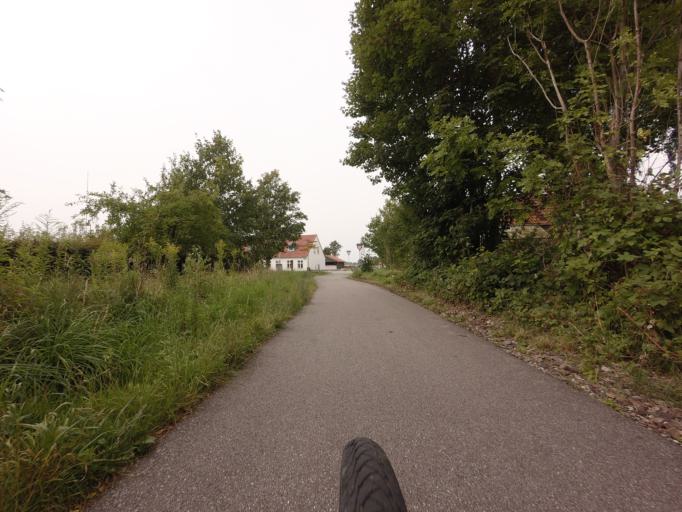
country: DK
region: Zealand
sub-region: Naestved Kommune
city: Fuglebjerg
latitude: 55.2647
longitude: 11.5187
